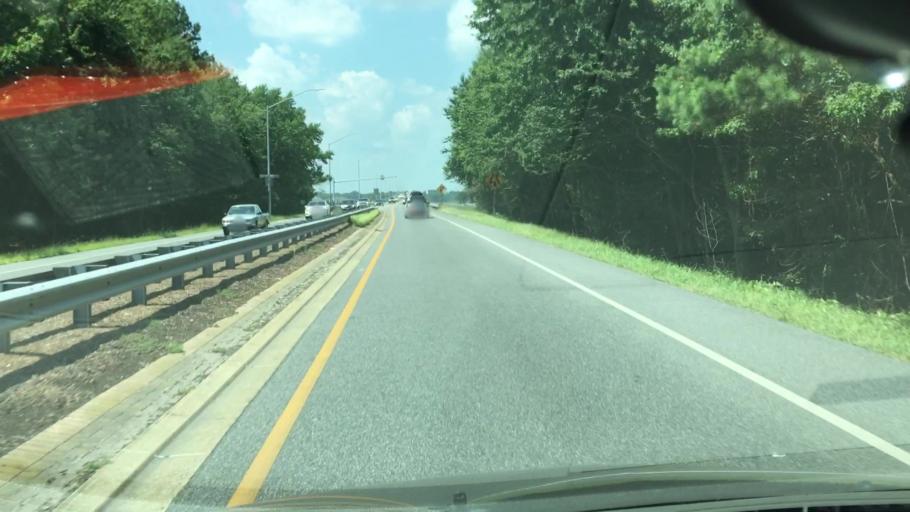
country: US
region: Maryland
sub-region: Worcester County
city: Ocean Pines
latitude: 38.3904
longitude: -75.1115
